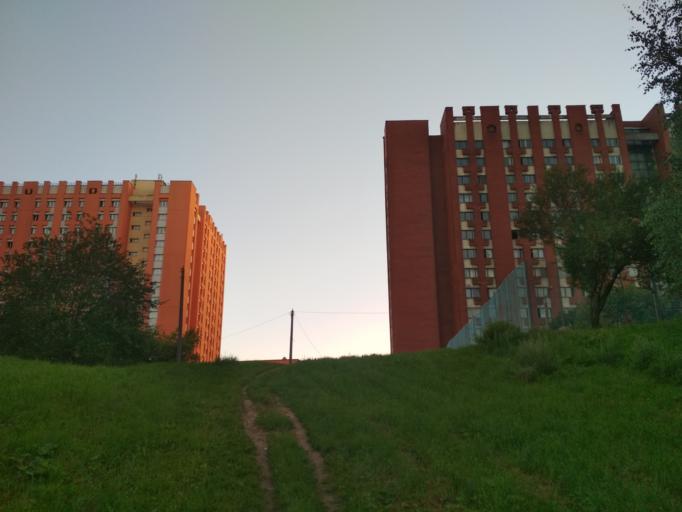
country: BY
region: Minsk
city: Minsk
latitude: 53.8903
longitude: 27.5657
